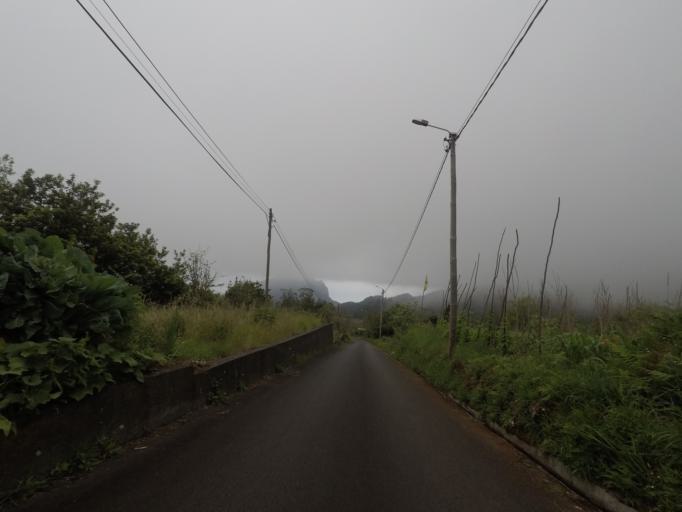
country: PT
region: Madeira
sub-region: Santana
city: Santana
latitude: 32.7493
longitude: -16.8776
